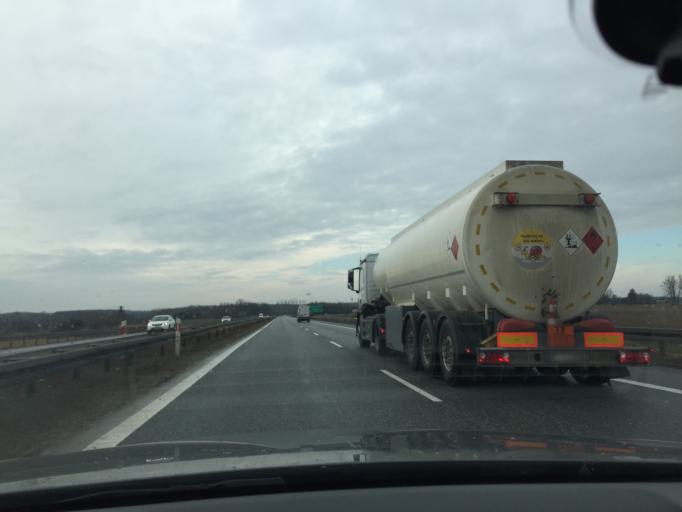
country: PL
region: Masovian Voivodeship
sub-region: Powiat zyrardowski
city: Mszczonow
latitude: 51.9661
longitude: 20.5009
